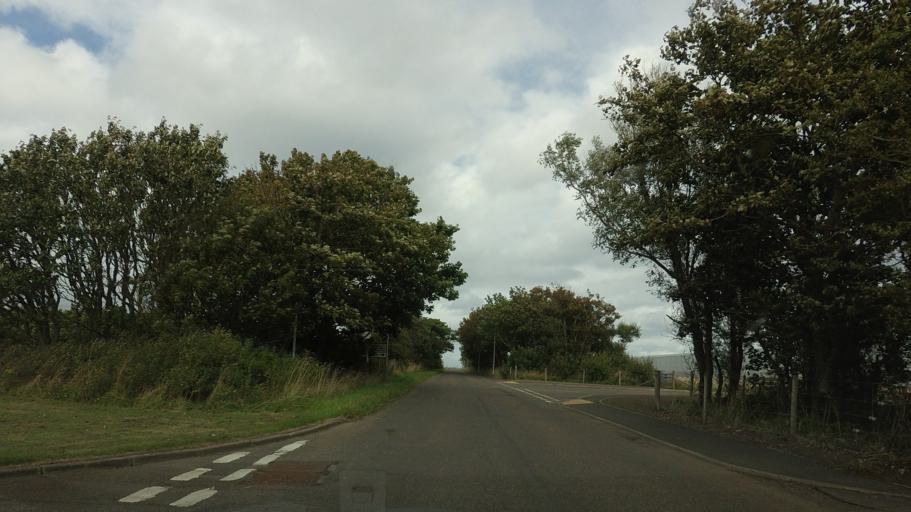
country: GB
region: Scotland
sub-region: Highland
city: Wick
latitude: 58.4509
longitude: -3.0873
